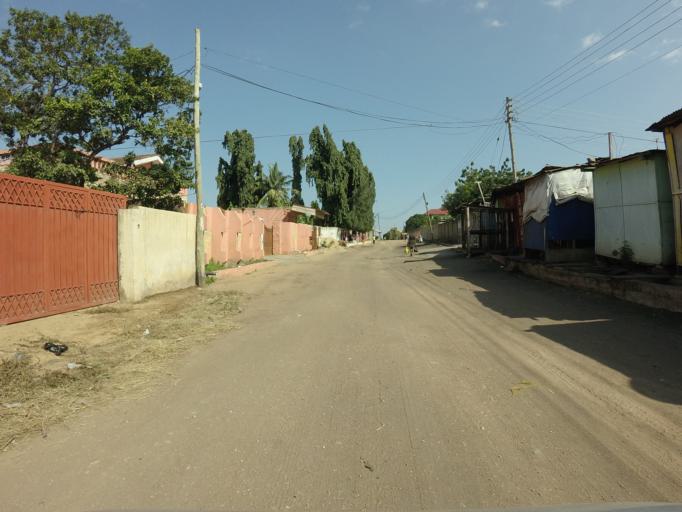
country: GH
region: Greater Accra
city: Dome
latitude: 5.6427
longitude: -0.2349
